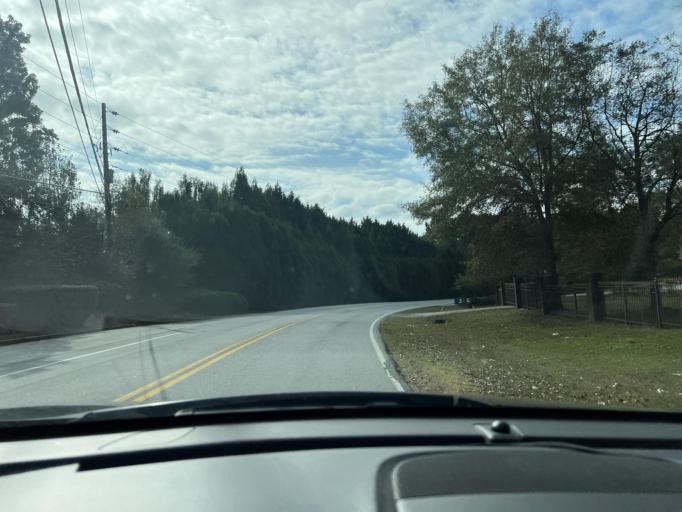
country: US
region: Georgia
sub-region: Gwinnett County
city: Grayson
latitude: 33.8926
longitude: -83.9917
